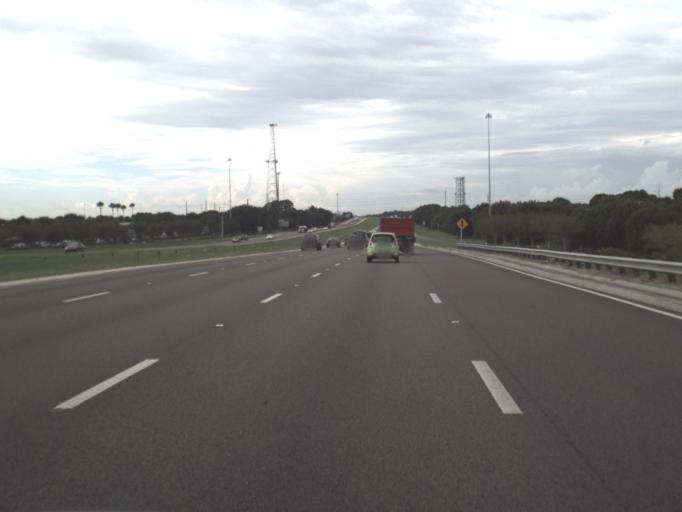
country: US
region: Florida
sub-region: Sarasota County
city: Fruitville
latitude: 27.3371
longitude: -82.4471
